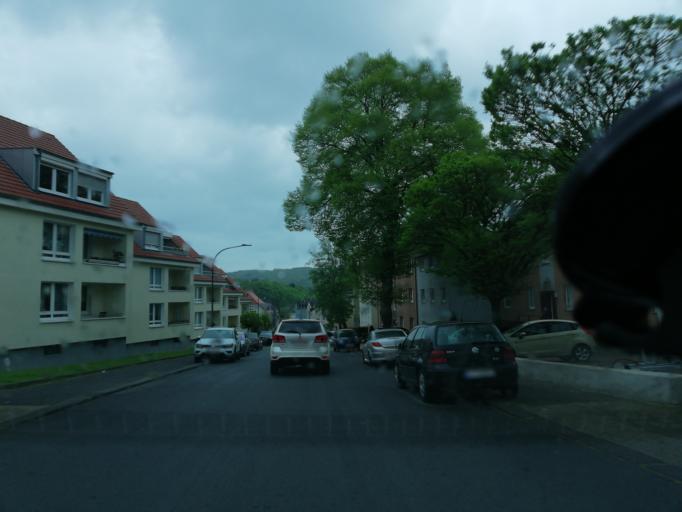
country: DE
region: North Rhine-Westphalia
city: Wulfrath
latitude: 51.2392
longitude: 7.0870
